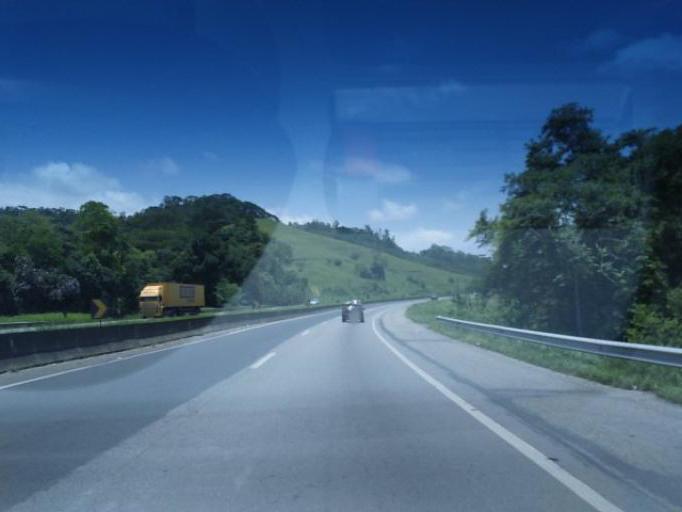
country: BR
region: Sao Paulo
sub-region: Miracatu
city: Miracatu
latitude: -24.2622
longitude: -47.3790
